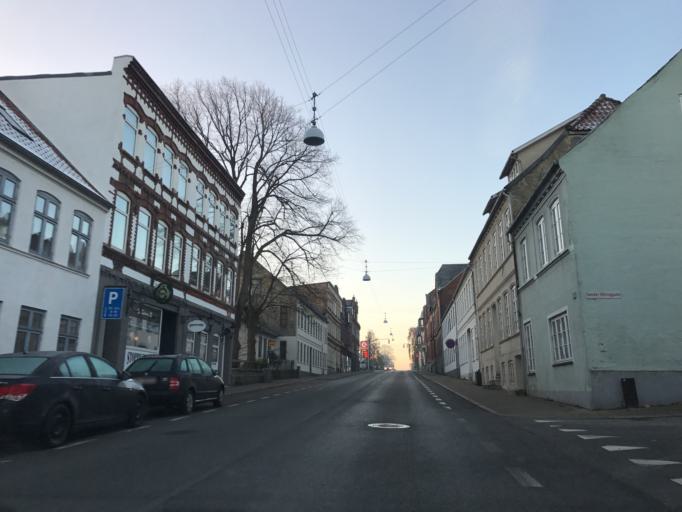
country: DK
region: South Denmark
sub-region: Haderslev Kommune
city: Haderslev
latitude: 55.2464
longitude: 9.4902
